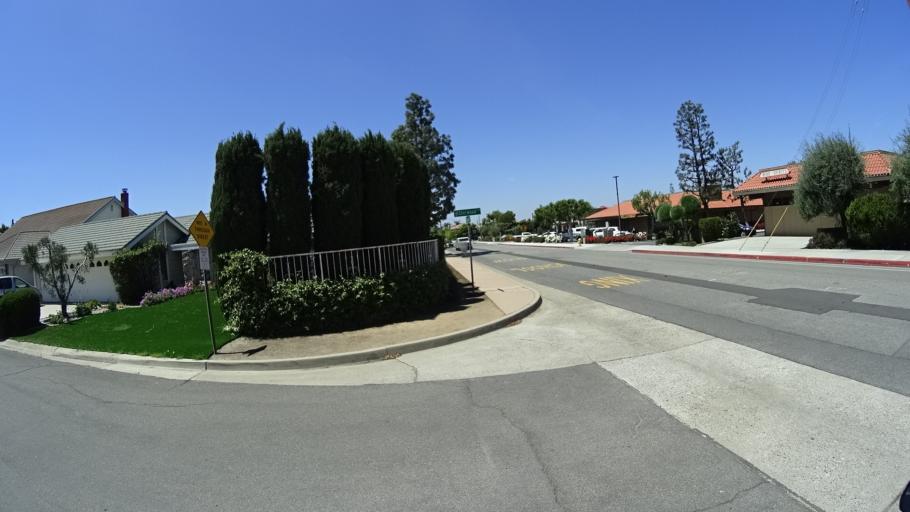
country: US
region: California
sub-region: Orange County
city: Villa Park
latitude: 33.8140
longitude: -117.8203
